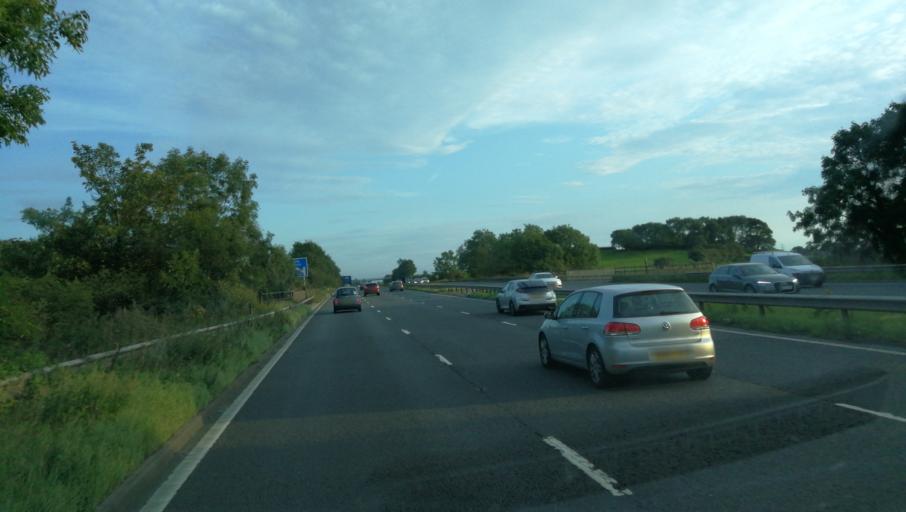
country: GB
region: England
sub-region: Lancashire
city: Galgate
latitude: 53.9983
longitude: -2.7803
